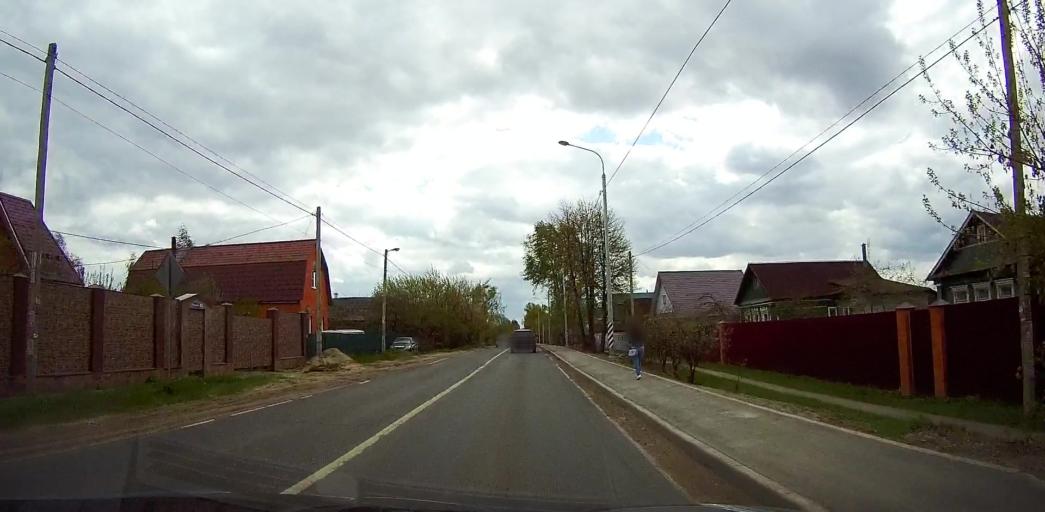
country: RU
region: Moskovskaya
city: Beloozerskiy
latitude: 55.4660
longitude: 38.4184
